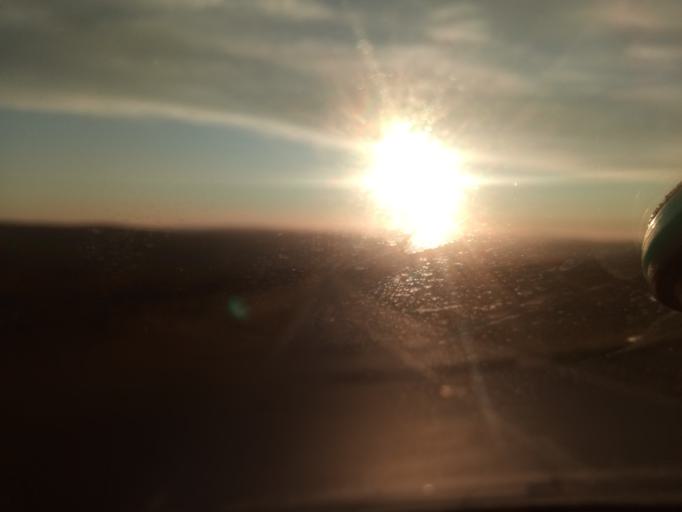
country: GB
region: England
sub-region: Northumberland
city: Bardon Mill
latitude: 54.7839
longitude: -2.3178
